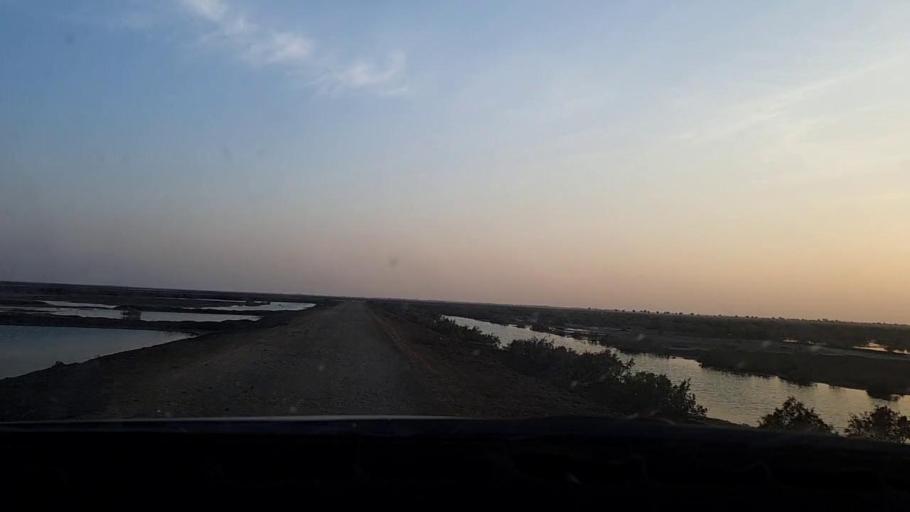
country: PK
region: Sindh
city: Tando Mittha Khan
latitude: 25.8463
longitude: 69.2303
